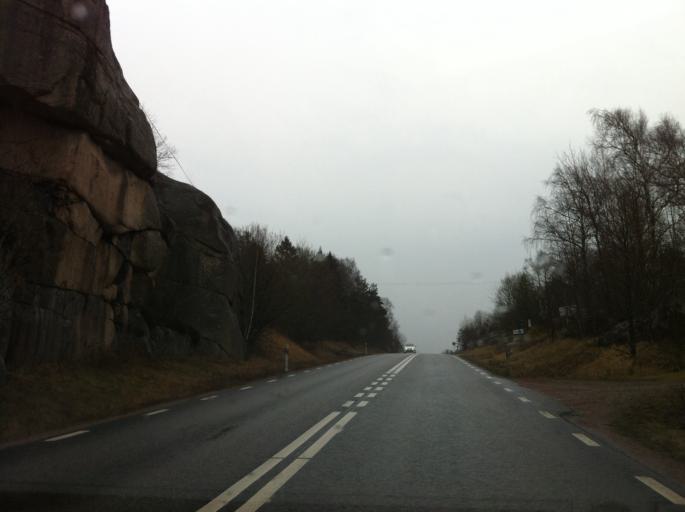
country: SE
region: Vaestra Goetaland
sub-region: Sotenas Kommun
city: Kungshamn
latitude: 58.3943
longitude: 11.2637
